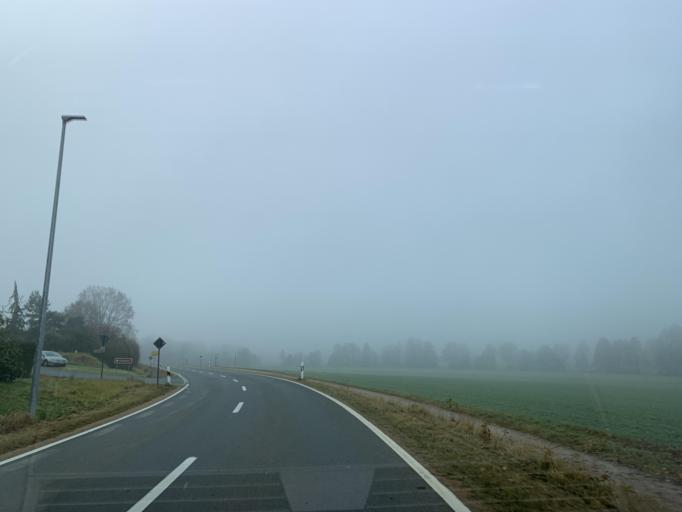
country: DE
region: Bavaria
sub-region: Upper Palatinate
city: Neunburg vorm Wald
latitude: 49.3605
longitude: 12.3986
